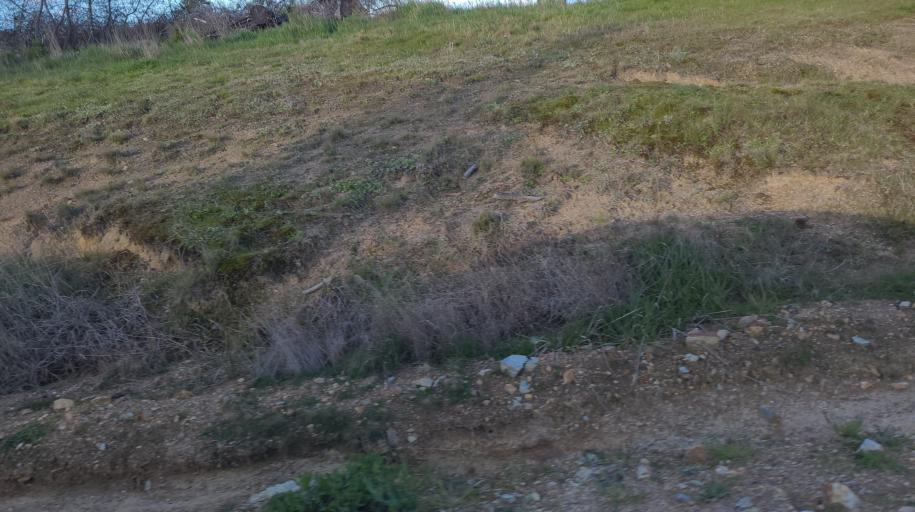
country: AU
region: New South Wales
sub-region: Blayney
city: Millthorpe
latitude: -33.4016
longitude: 149.3158
